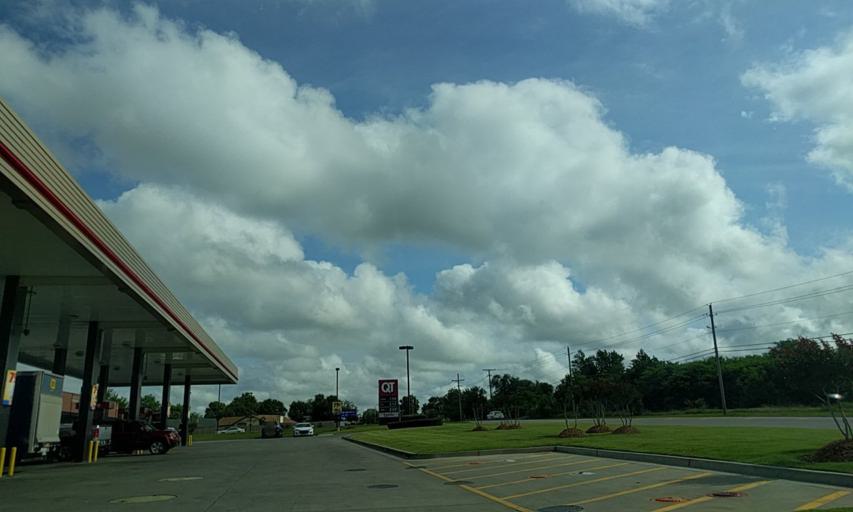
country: US
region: Oklahoma
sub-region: Tulsa County
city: Owasso
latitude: 36.2934
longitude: -95.8485
